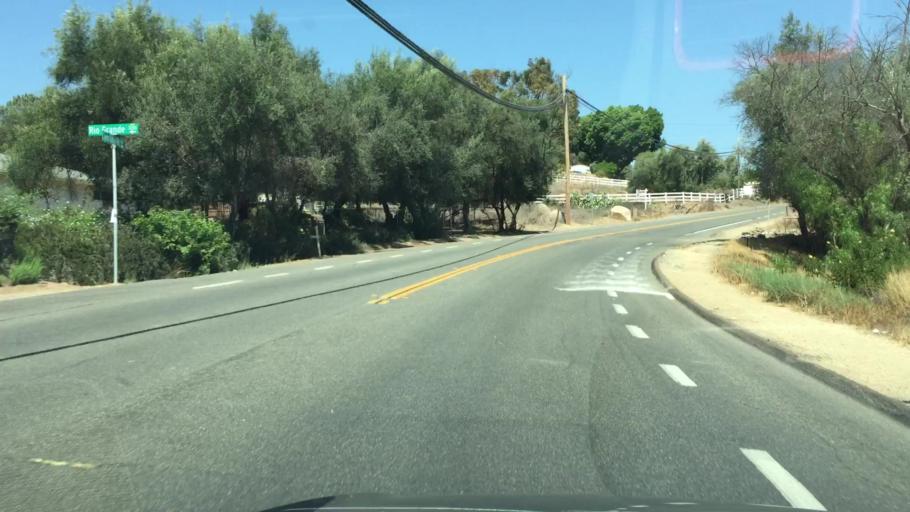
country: US
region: California
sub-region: San Diego County
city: Jamul
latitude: 32.7291
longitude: -116.8639
